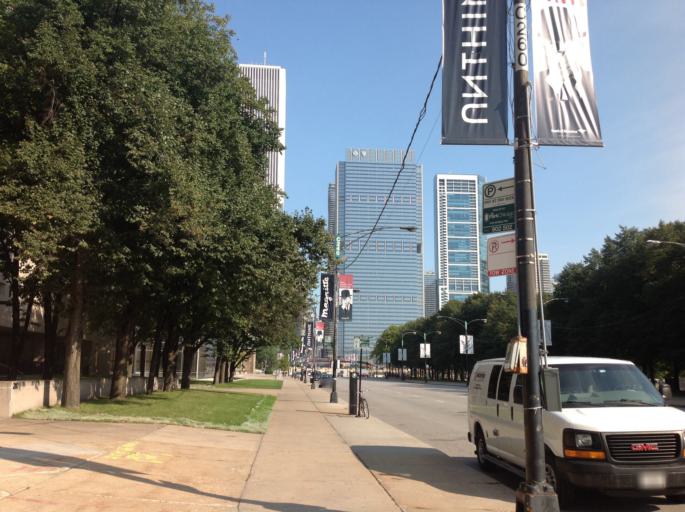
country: US
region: Illinois
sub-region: Cook County
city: Chicago
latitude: 41.8786
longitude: -87.6209
